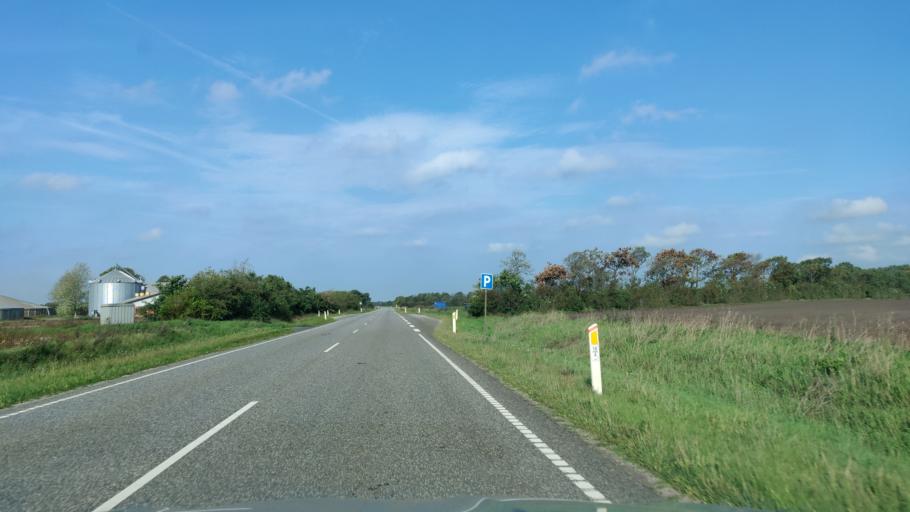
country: DK
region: Central Jutland
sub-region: Herning Kommune
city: Sunds
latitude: 56.2586
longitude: 9.0365
